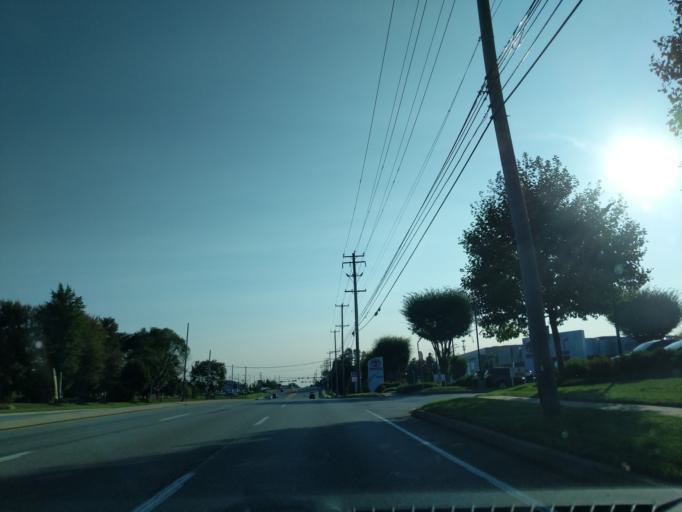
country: US
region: Pennsylvania
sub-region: Delaware County
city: Chester Heights
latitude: 39.8816
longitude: -75.5408
